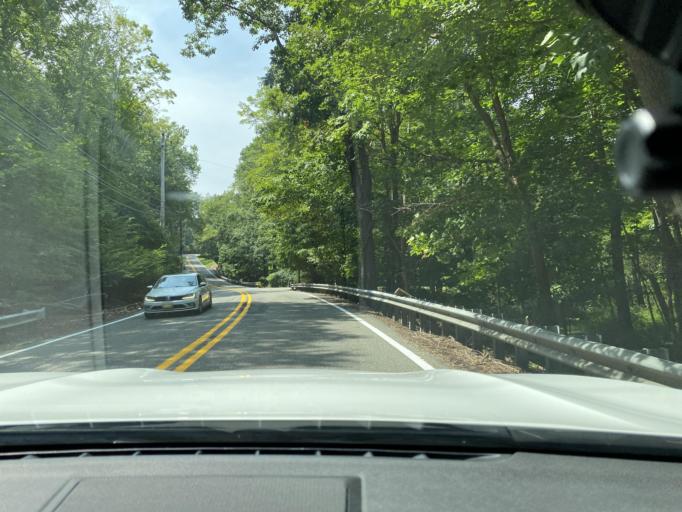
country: US
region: New Jersey
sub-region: Bergen County
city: Franklin Lakes
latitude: 41.0580
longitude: -74.2127
